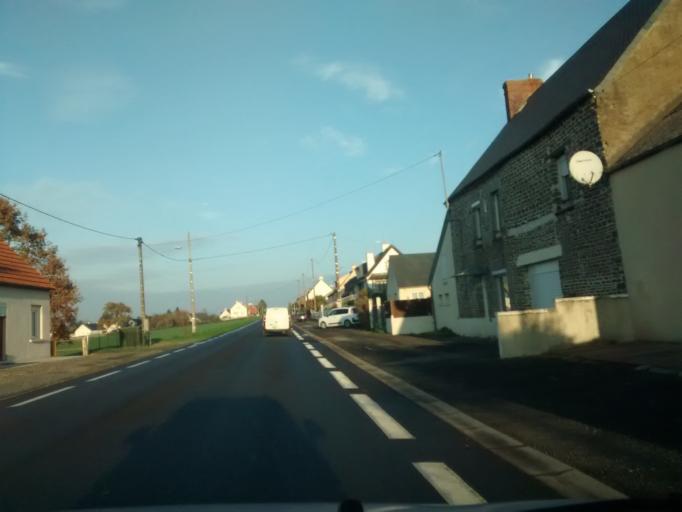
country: FR
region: Lower Normandy
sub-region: Departement de la Manche
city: Pontorson
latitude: 48.5419
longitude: -1.4961
